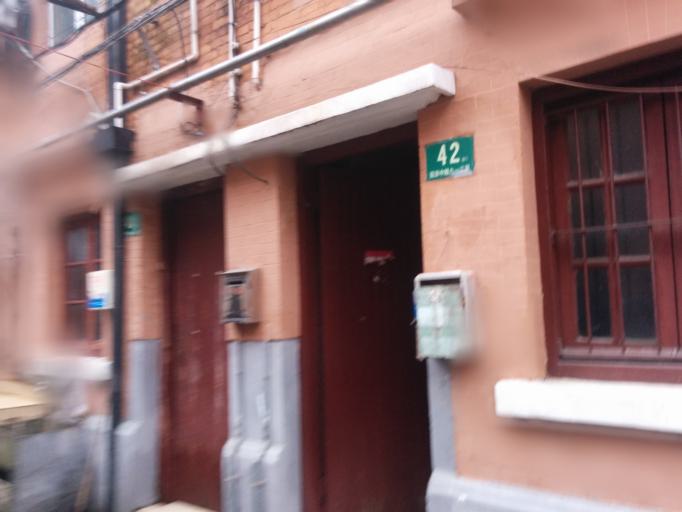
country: CN
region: Shanghai Shi
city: Shanghai
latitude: 31.2241
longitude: 121.4486
